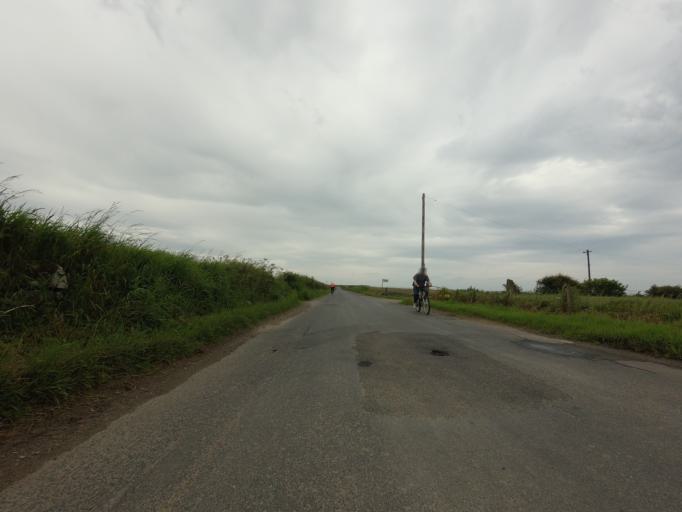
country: GB
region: Scotland
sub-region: Aberdeenshire
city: Whitehills
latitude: 57.6703
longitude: -2.6046
